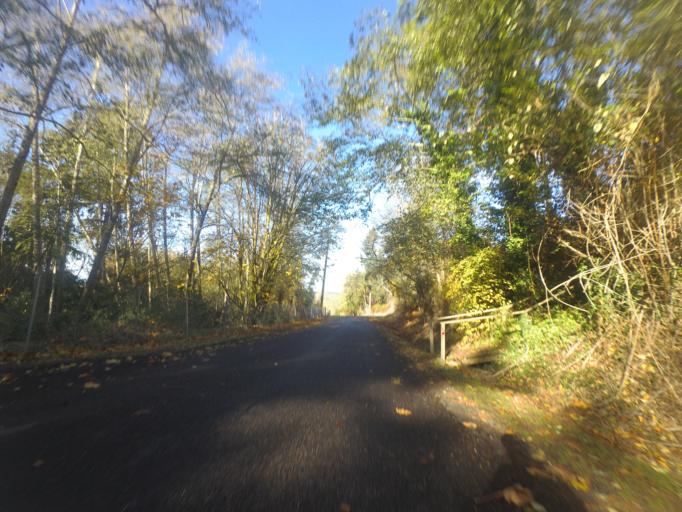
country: US
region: Washington
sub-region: Pierce County
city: University Place
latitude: 47.2347
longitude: -122.5571
